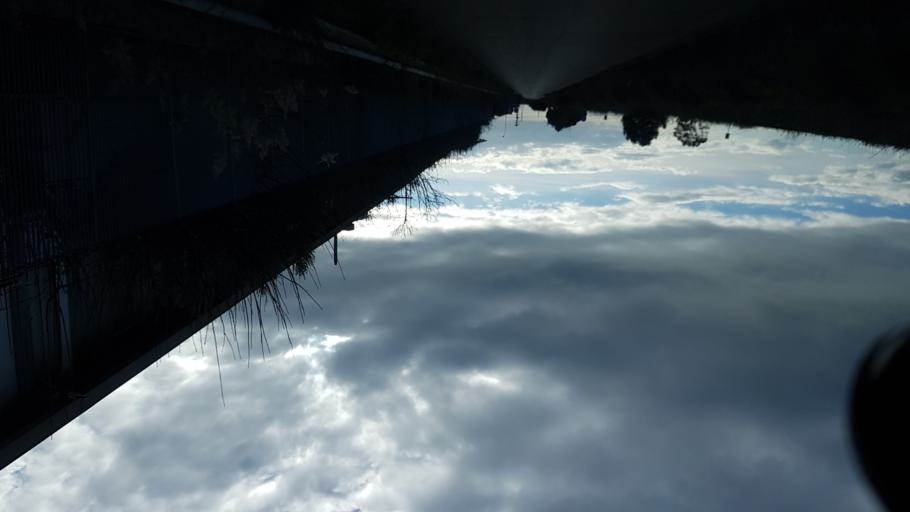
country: IT
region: Apulia
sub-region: Provincia di Brindisi
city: La Rosa
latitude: 40.6157
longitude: 17.9542
